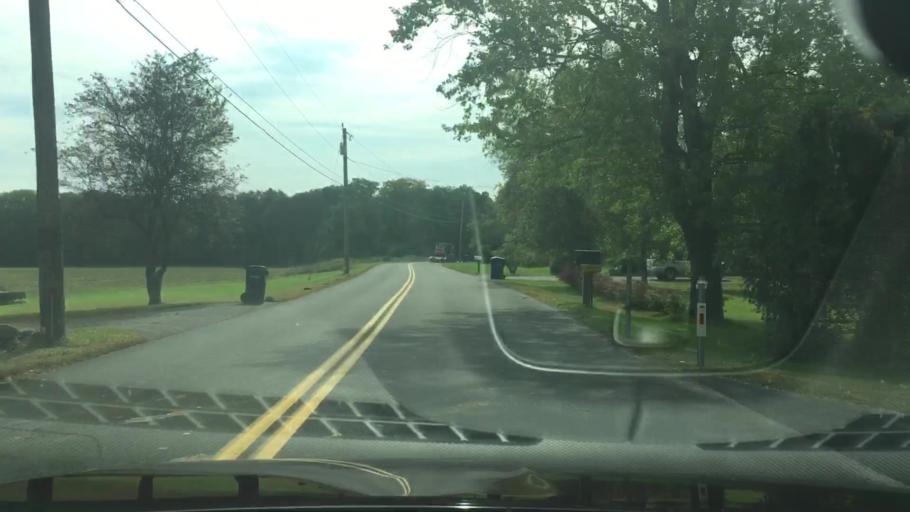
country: US
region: Connecticut
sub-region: Tolland County
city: Ellington
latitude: 41.9468
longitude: -72.4816
